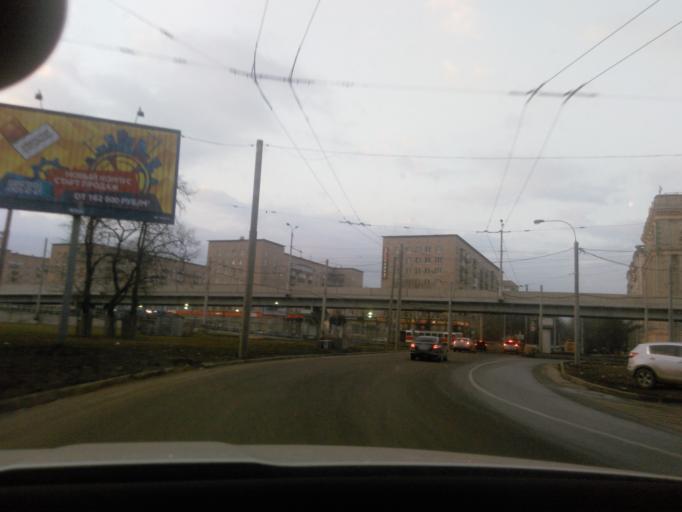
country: RU
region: Moscow
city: Sokol
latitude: 55.8076
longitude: 37.5068
